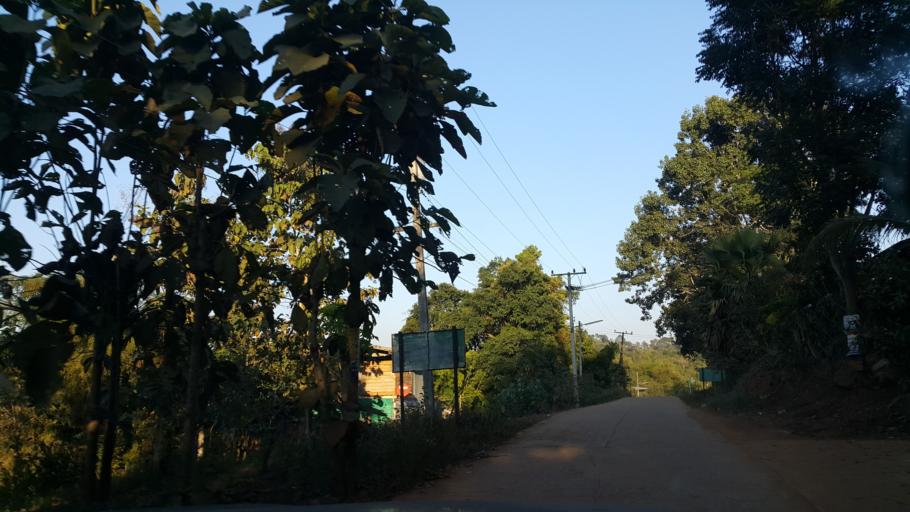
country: TH
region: Sukhothai
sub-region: Amphoe Si Satchanalai
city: Si Satchanalai
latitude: 17.6197
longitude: 99.6228
